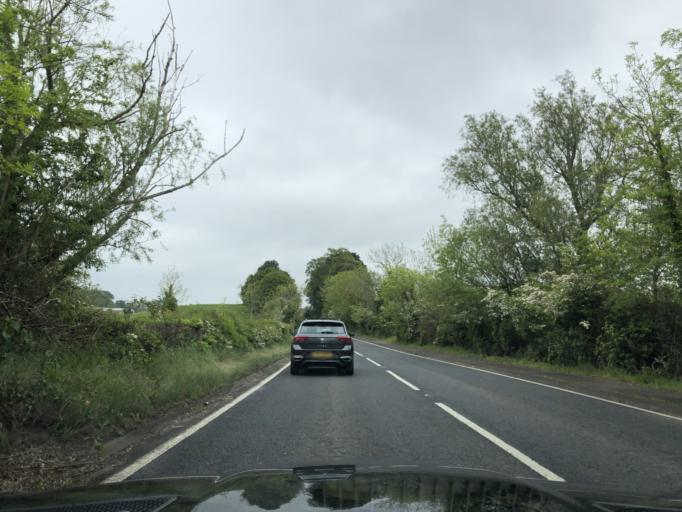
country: GB
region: Northern Ireland
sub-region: Down District
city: Downpatrick
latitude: 54.3202
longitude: -5.7236
